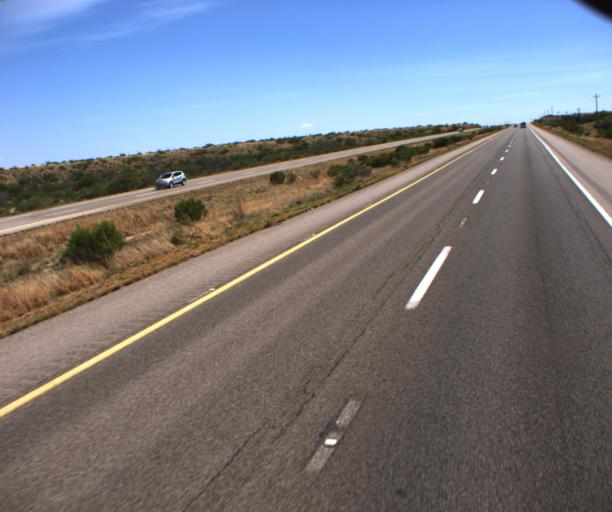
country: US
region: Arizona
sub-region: Cochise County
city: Whetstone
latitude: 31.9328
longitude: -110.3414
